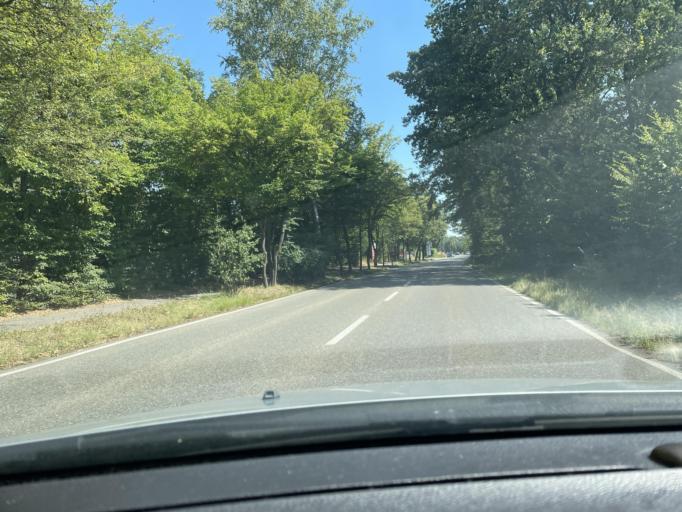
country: DE
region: Bavaria
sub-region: Upper Bavaria
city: Waldkraiburg
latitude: 48.2067
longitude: 12.4140
